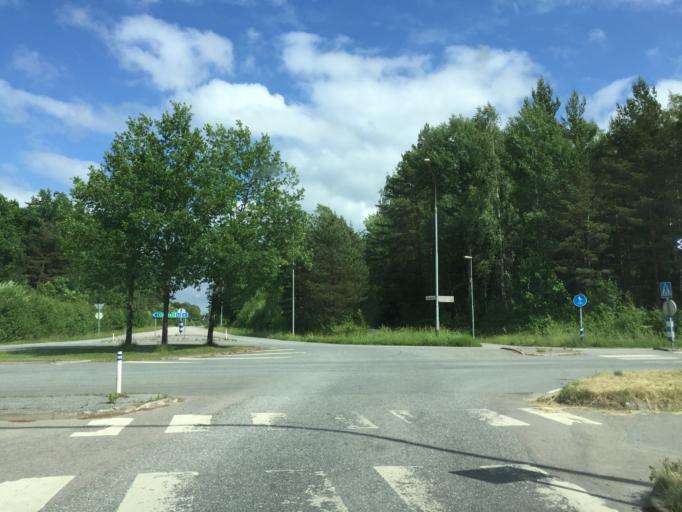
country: SE
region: OErebro
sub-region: Orebro Kommun
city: Orebro
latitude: 59.2430
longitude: 15.1965
